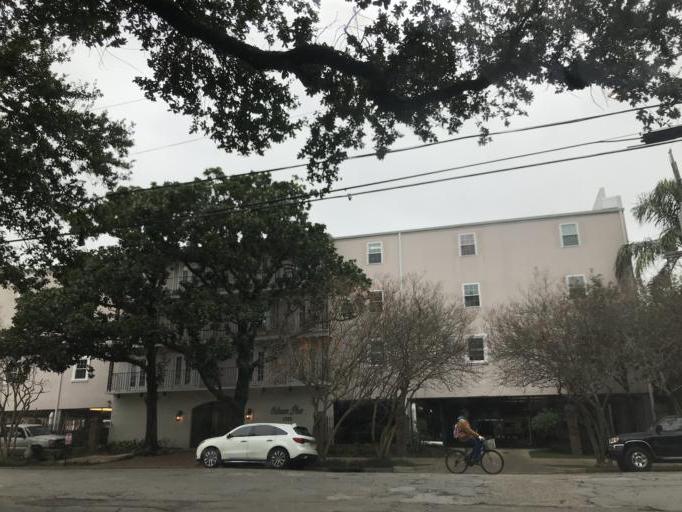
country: US
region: Louisiana
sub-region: Orleans Parish
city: New Orleans
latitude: 29.9349
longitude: -90.0746
